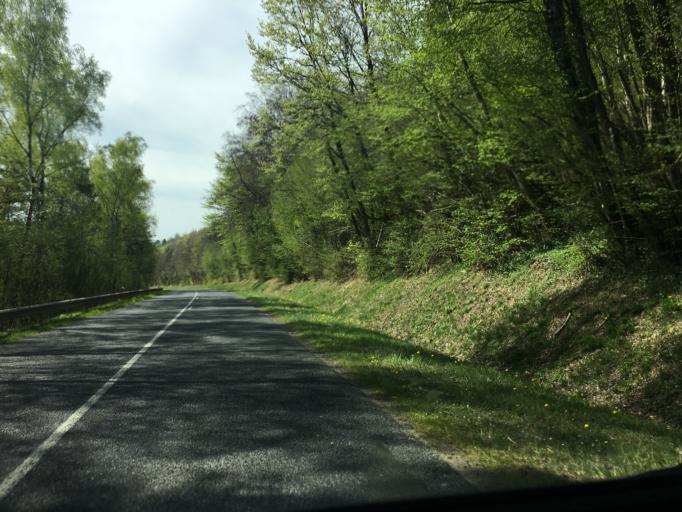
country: FR
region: Lorraine
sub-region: Departement de la Meuse
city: Lerouville
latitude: 48.8439
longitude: 5.5091
